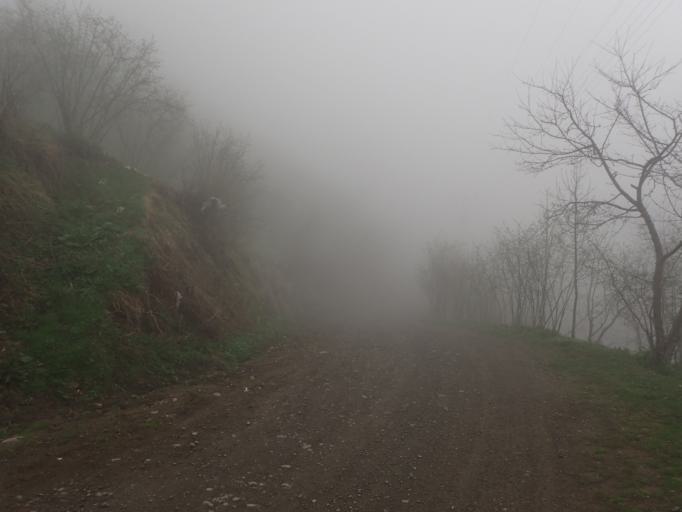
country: TR
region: Ordu
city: Korgan
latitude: 40.7796
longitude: 37.2962
